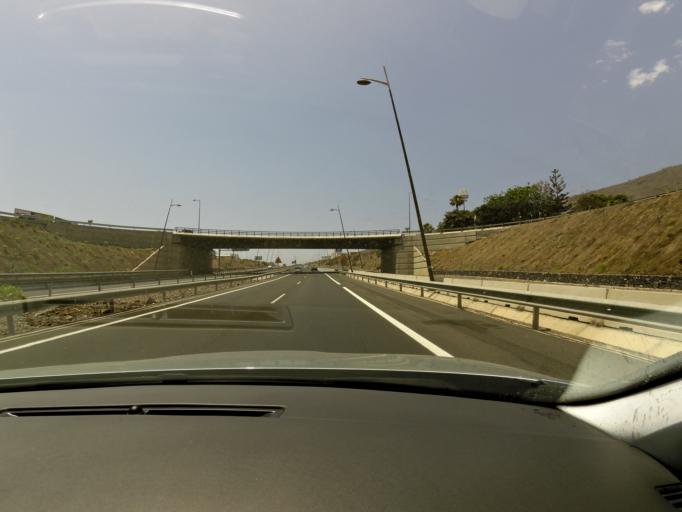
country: ES
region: Canary Islands
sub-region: Provincia de Santa Cruz de Tenerife
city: Adeje
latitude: 28.1224
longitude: -16.7401
